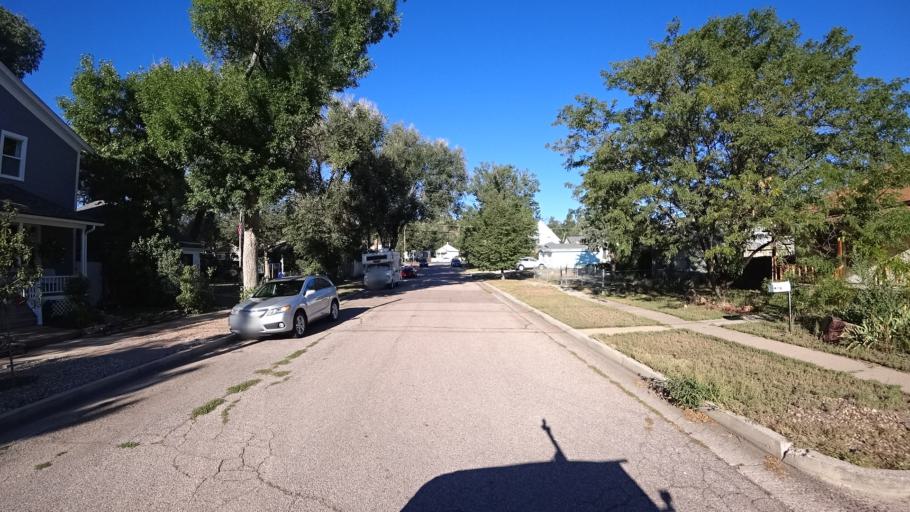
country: US
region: Colorado
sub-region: El Paso County
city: Colorado Springs
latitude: 38.8416
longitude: -104.8313
